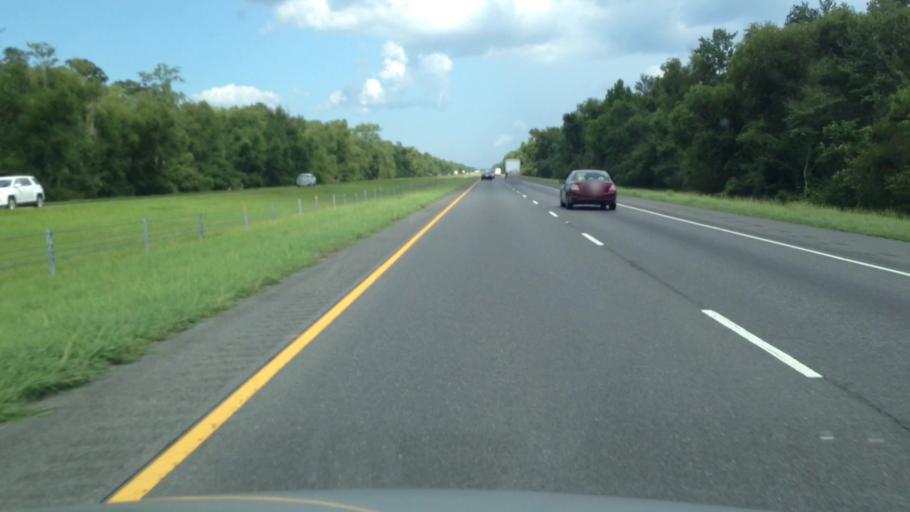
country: US
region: Louisiana
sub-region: Saint James Parish
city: Grand Point
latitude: 30.1381
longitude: -90.7416
